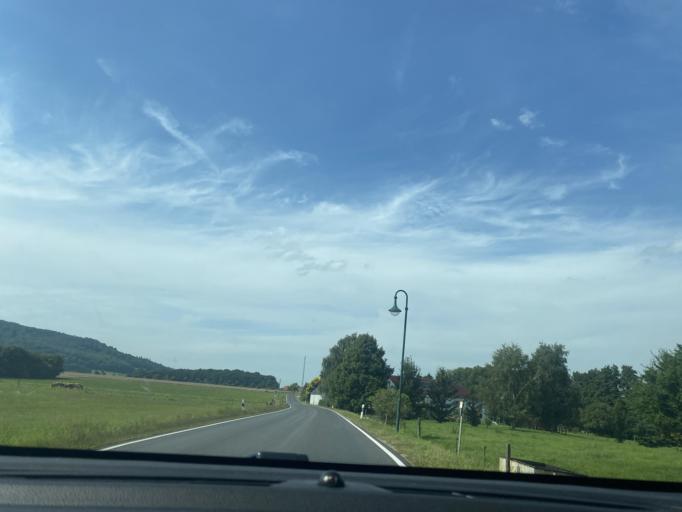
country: DE
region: Saxony
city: Sohland am Rotstein
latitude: 51.0954
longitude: 14.7922
